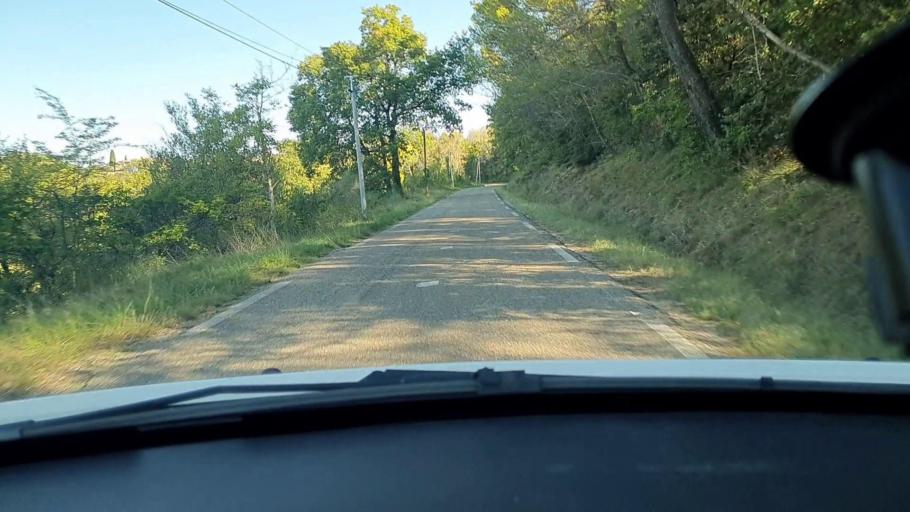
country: FR
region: Languedoc-Roussillon
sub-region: Departement du Gard
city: Saint-Julien-de-Peyrolas
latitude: 44.2572
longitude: 4.5241
